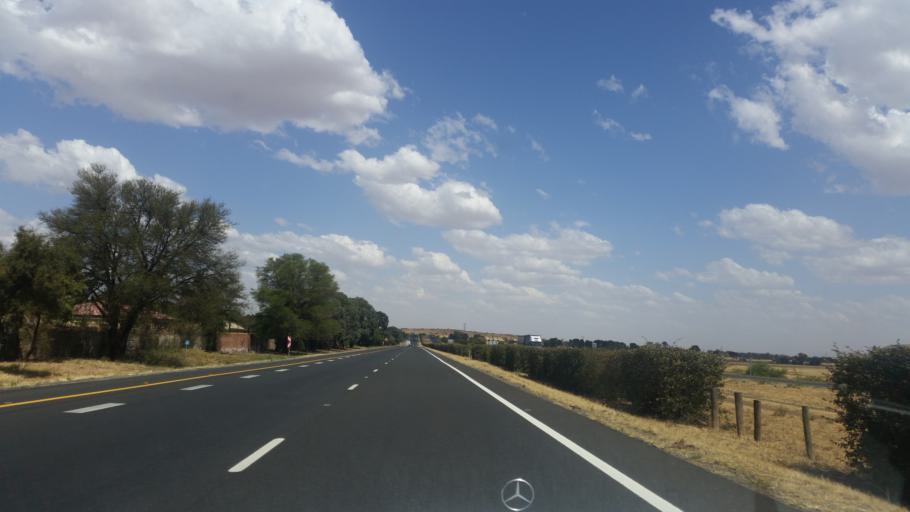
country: ZA
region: Orange Free State
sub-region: Mangaung Metropolitan Municipality
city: Bloemfontein
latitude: -29.1702
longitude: 26.1843
